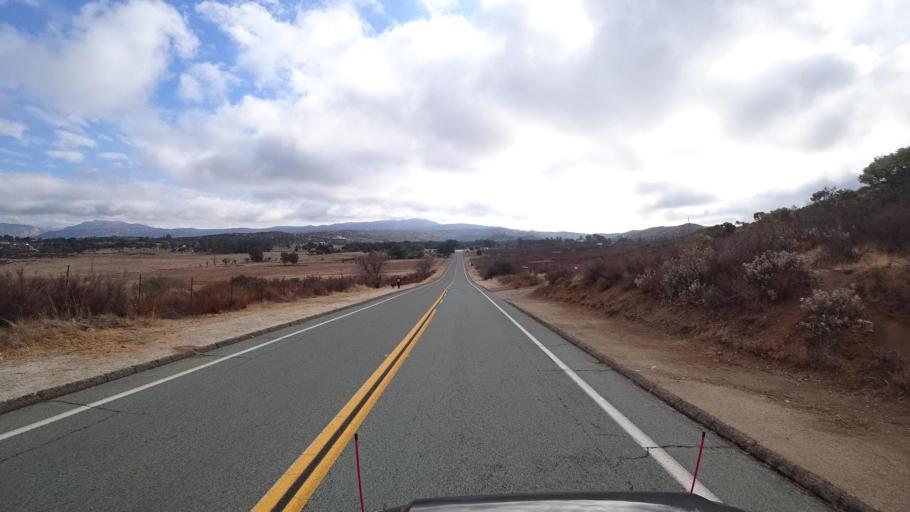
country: MX
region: Baja California
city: Tecate
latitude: 32.6151
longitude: -116.6047
